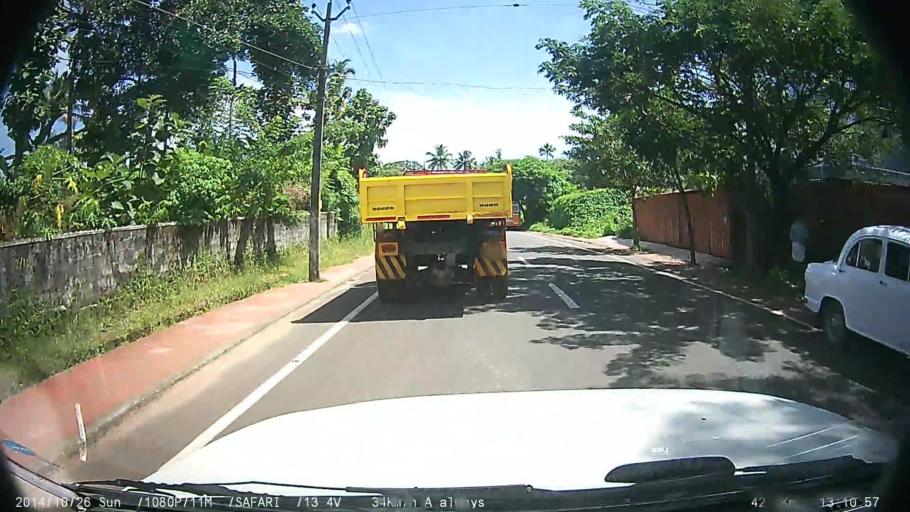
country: IN
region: Kerala
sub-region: Kottayam
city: Changanacheri
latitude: 9.4525
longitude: 76.5442
